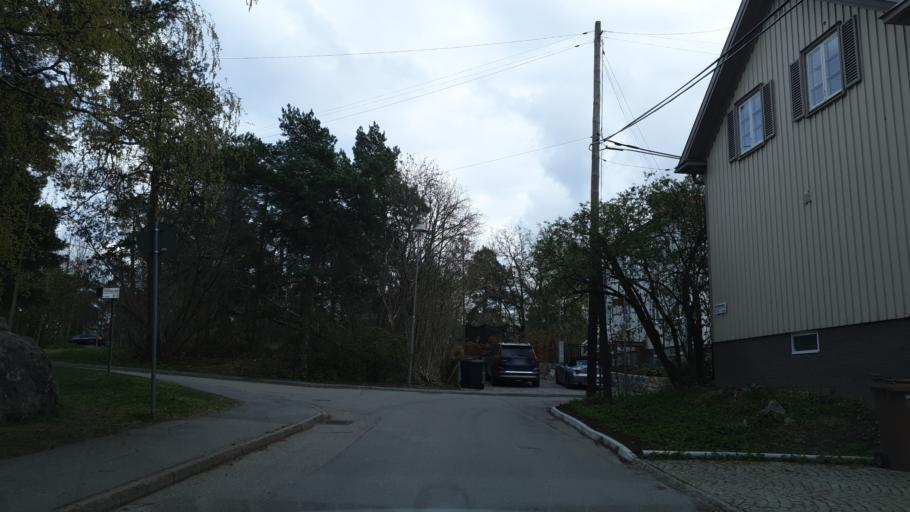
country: SE
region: Stockholm
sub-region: Sundbybergs Kommun
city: Sundbyberg
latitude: 59.3324
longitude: 17.9703
